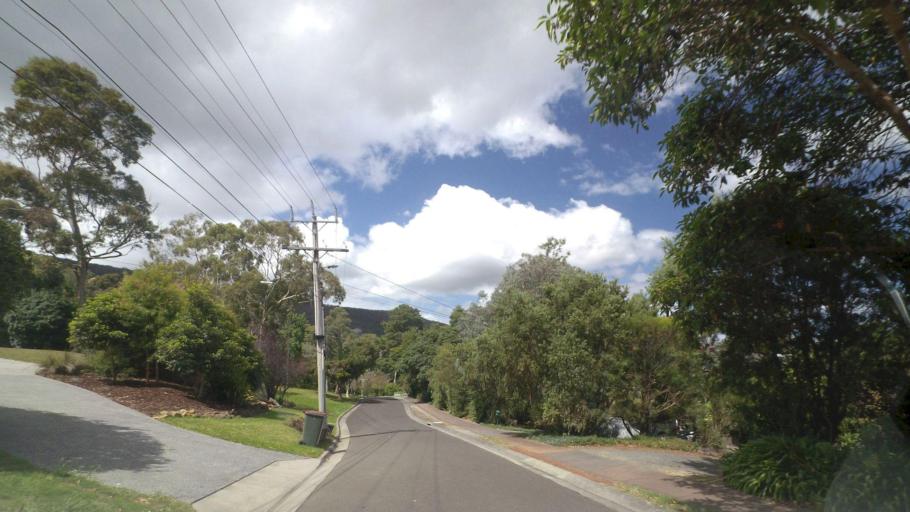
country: AU
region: Victoria
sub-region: Knox
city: Ferntree Gully
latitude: -37.8692
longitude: 145.3026
